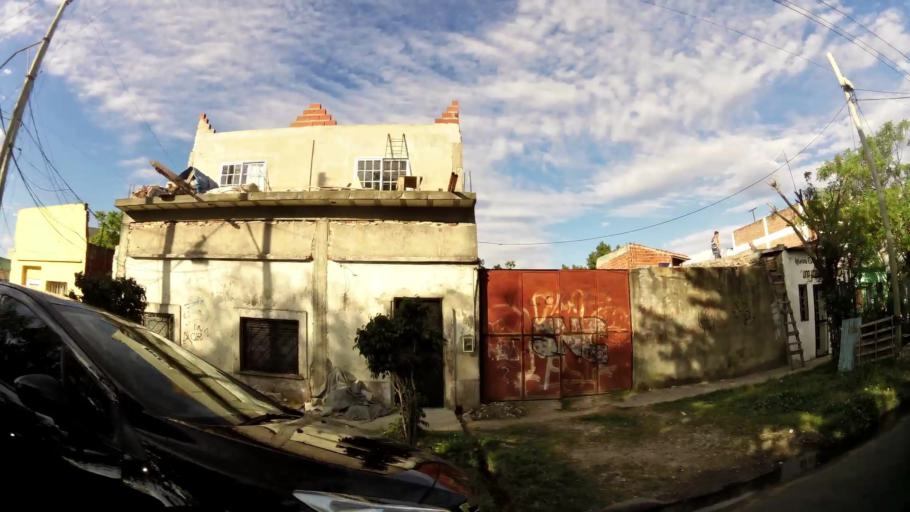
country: AR
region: Buenos Aires
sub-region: Partido de Lanus
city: Lanus
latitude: -34.7094
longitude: -58.3509
